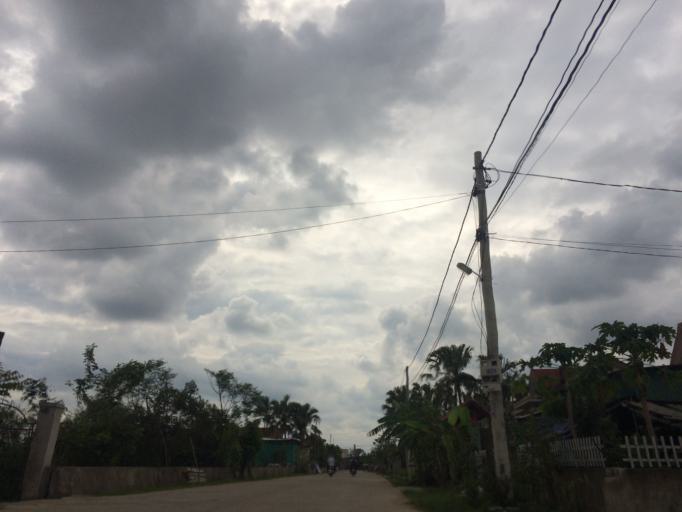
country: VN
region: Ha Tinh
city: Ha Tinh
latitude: 18.3455
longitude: 105.9222
